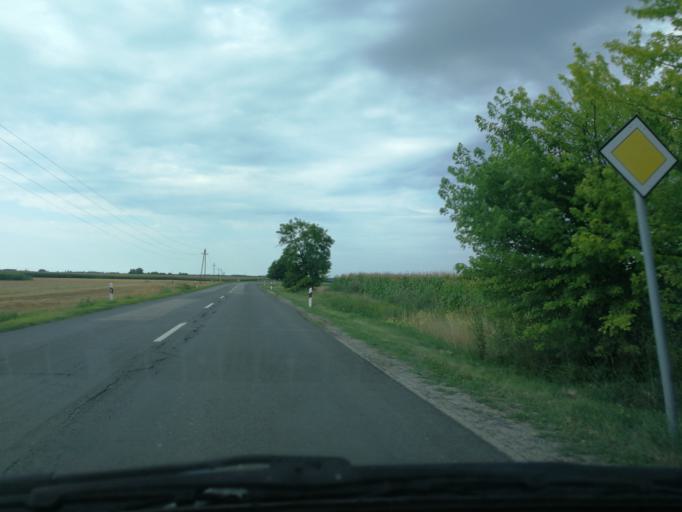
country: HU
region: Bacs-Kiskun
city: Dusnok
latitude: 46.4272
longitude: 18.9449
